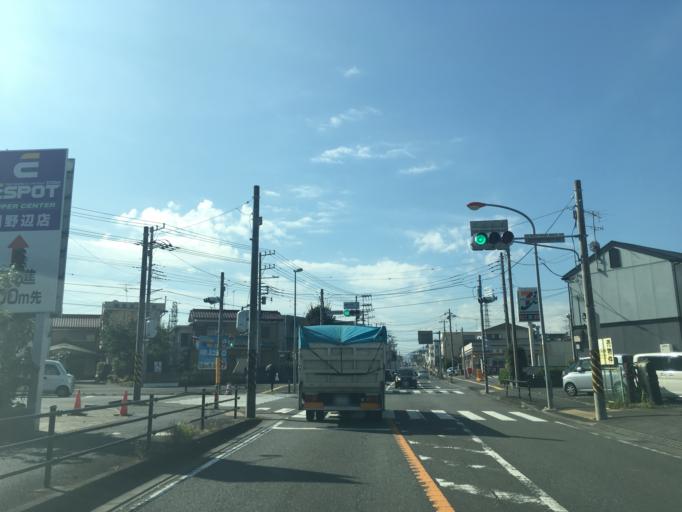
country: JP
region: Tokyo
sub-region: Machida-shi
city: Machida
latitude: 35.5743
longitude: 139.4067
